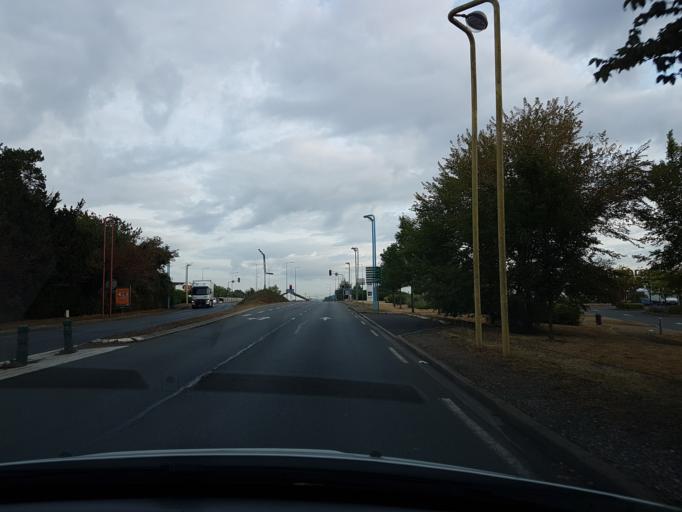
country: FR
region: Centre
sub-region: Departement d'Indre-et-Loire
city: Chambray-les-Tours
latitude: 47.3431
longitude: 0.7028
